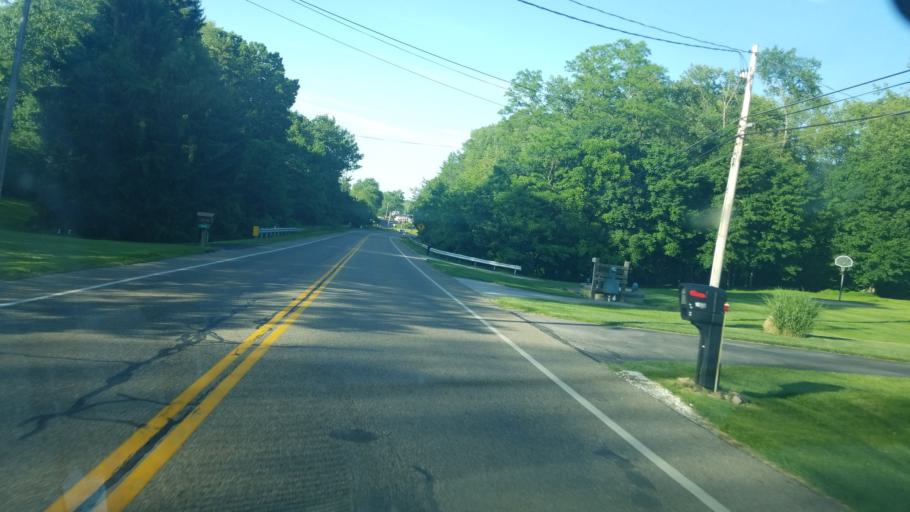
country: US
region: Ohio
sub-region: Portage County
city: Kent
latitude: 41.1329
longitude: -81.3960
